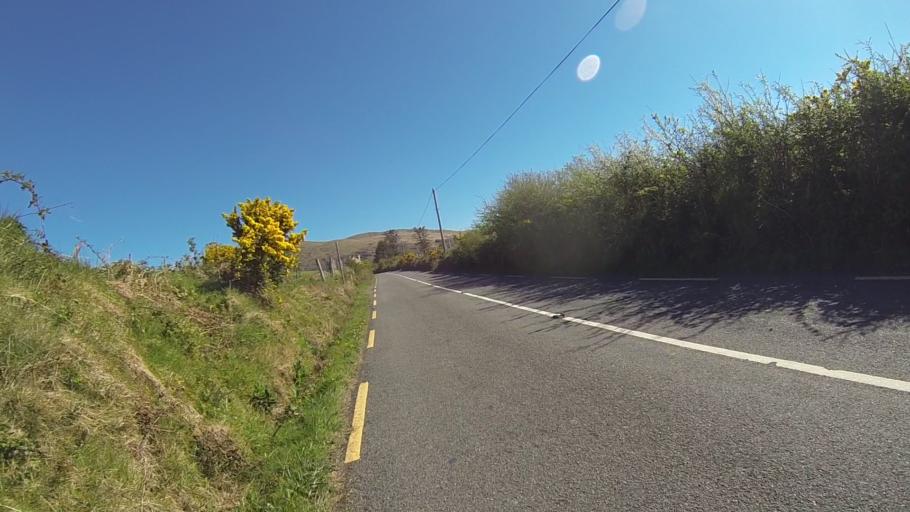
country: IE
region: Munster
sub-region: Ciarrai
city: Kenmare
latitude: 51.7758
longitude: -9.7307
